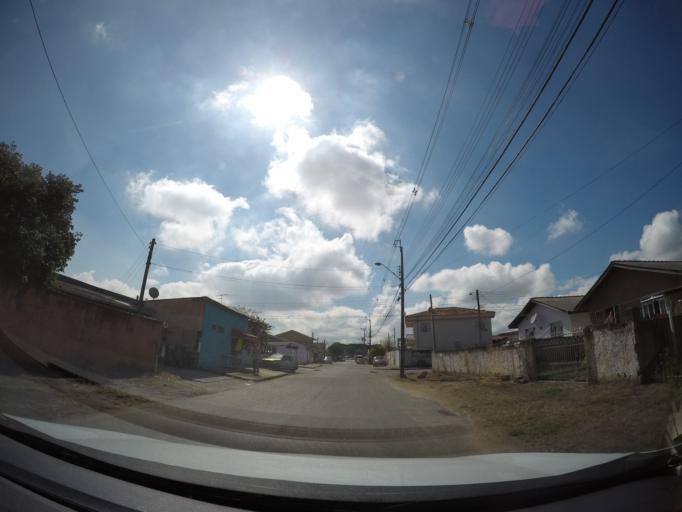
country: BR
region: Parana
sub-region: Sao Jose Dos Pinhais
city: Sao Jose dos Pinhais
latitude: -25.5011
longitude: -49.2179
